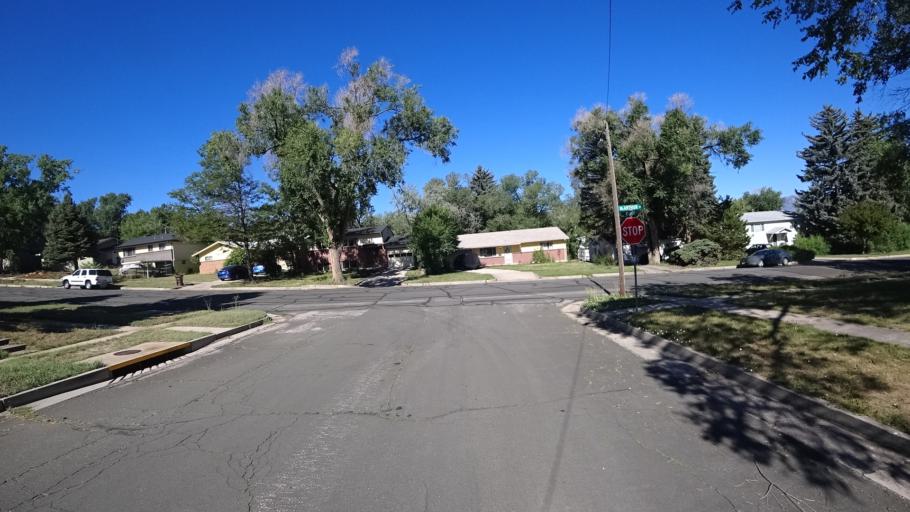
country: US
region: Colorado
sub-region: El Paso County
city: Colorado Springs
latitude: 38.8516
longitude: -104.7841
